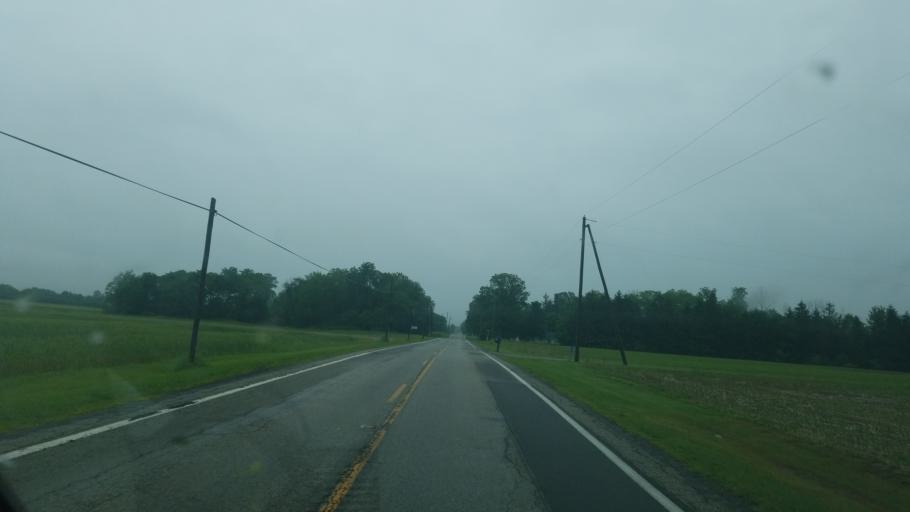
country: US
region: Ohio
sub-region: Crawford County
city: Bucyrus
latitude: 40.8421
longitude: -82.8754
